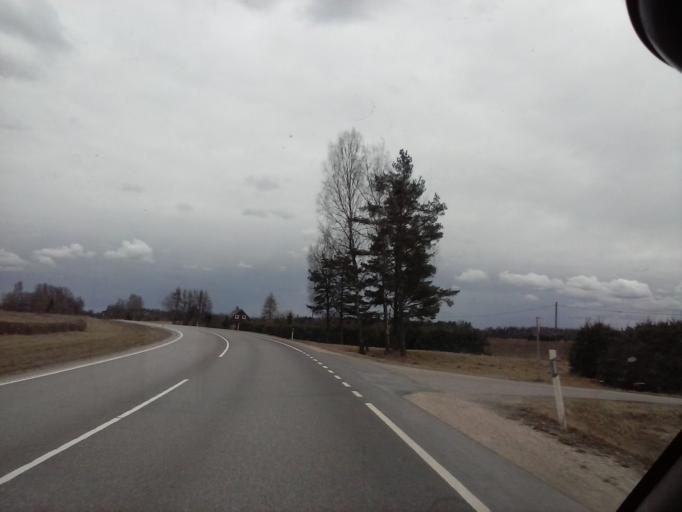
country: EE
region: Harju
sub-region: Anija vald
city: Kehra
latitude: 59.1144
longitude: 25.3139
